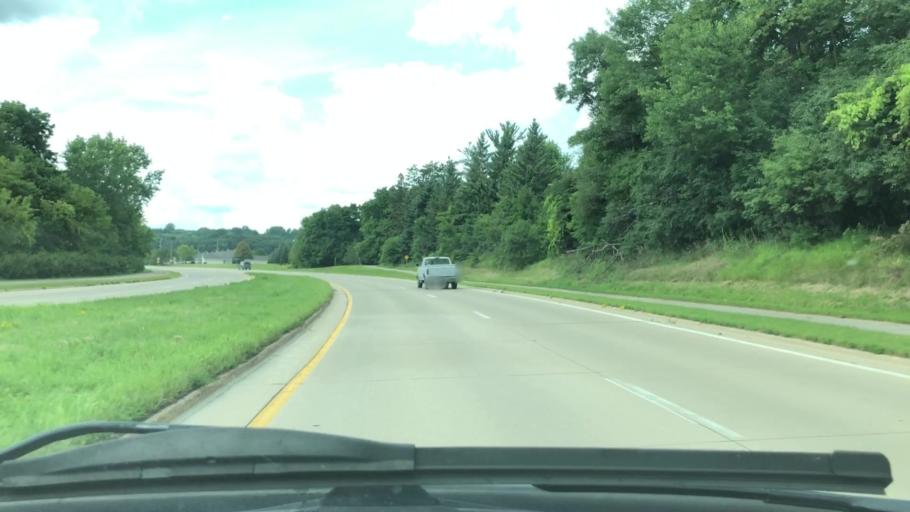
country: US
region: Minnesota
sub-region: Olmsted County
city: Rochester
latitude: 44.0011
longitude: -92.5018
